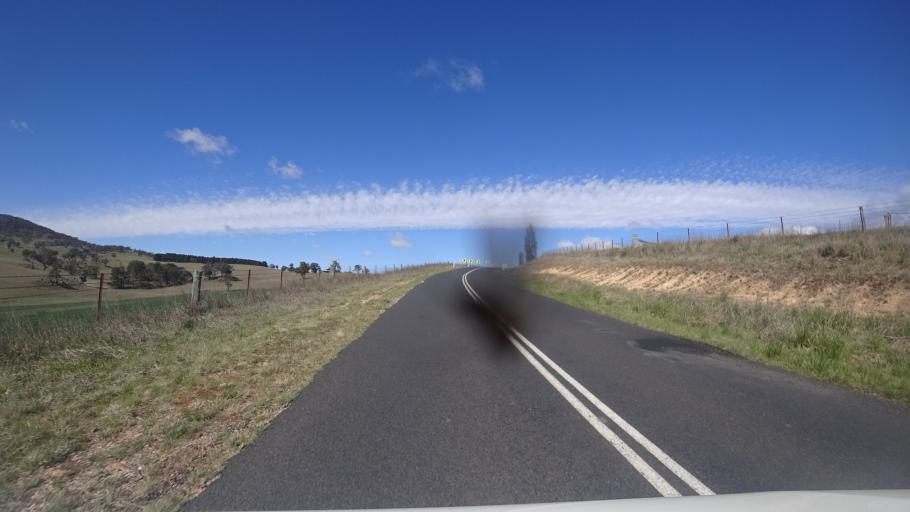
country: AU
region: New South Wales
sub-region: Lithgow
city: Portland
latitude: -33.5185
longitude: 149.9519
